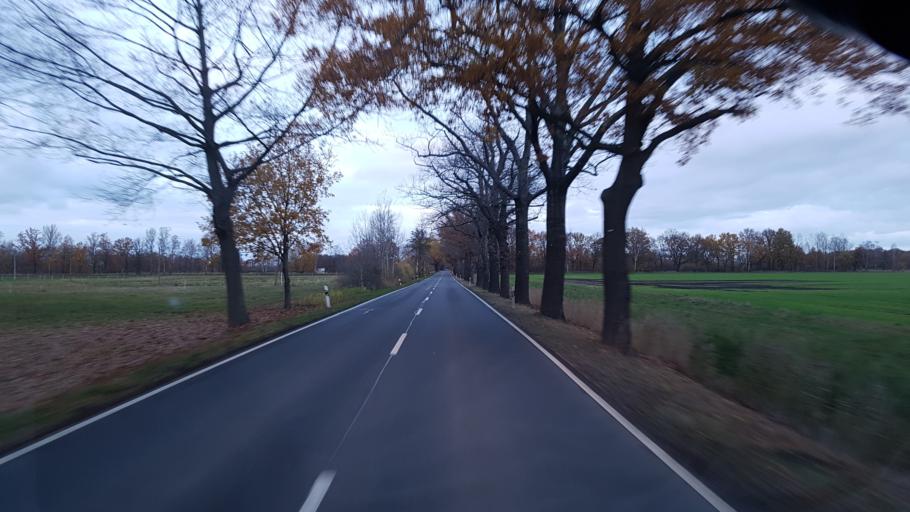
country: DE
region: Brandenburg
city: Schraden
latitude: 51.4506
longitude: 13.7111
